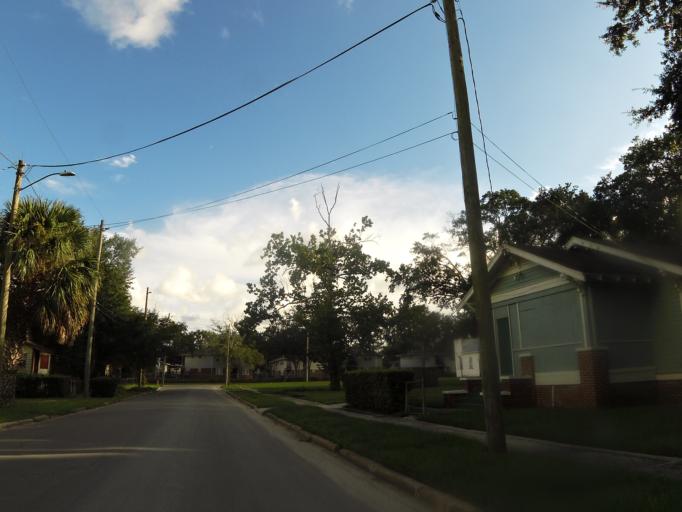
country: US
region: Florida
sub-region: Duval County
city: Jacksonville
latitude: 30.3426
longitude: -81.6649
